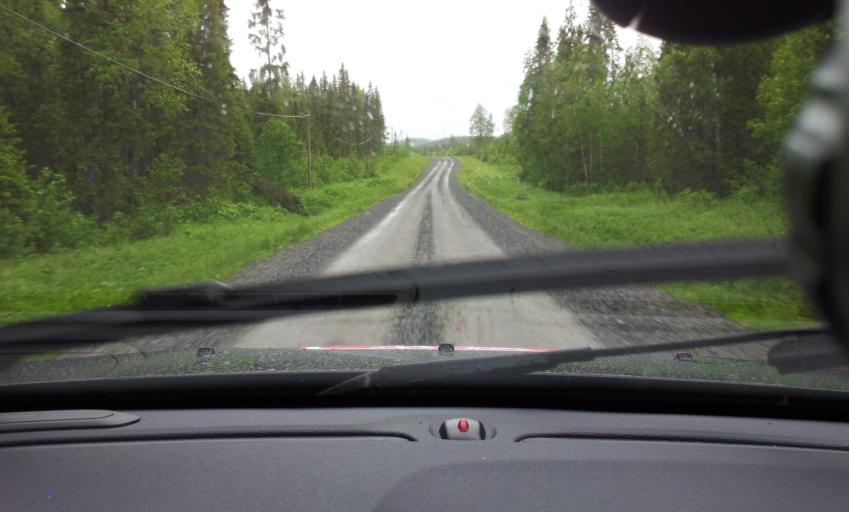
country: SE
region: Jaemtland
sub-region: Are Kommun
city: Are
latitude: 63.4947
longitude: 12.7655
